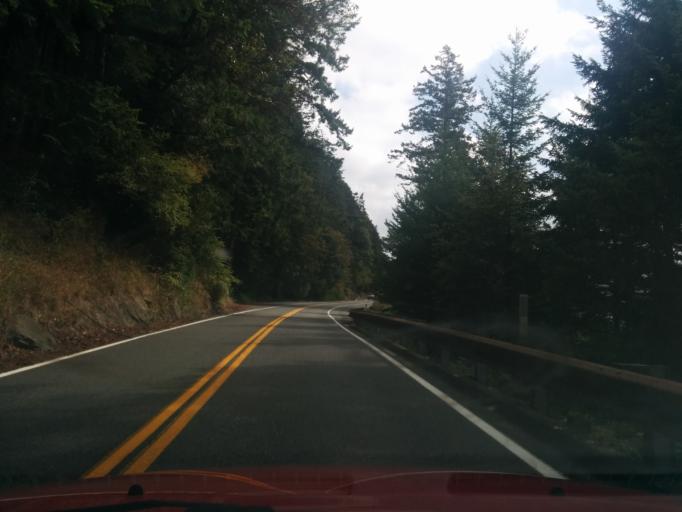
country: US
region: Washington
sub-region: Whatcom County
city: Bellingham
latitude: 48.6406
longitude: -122.4793
